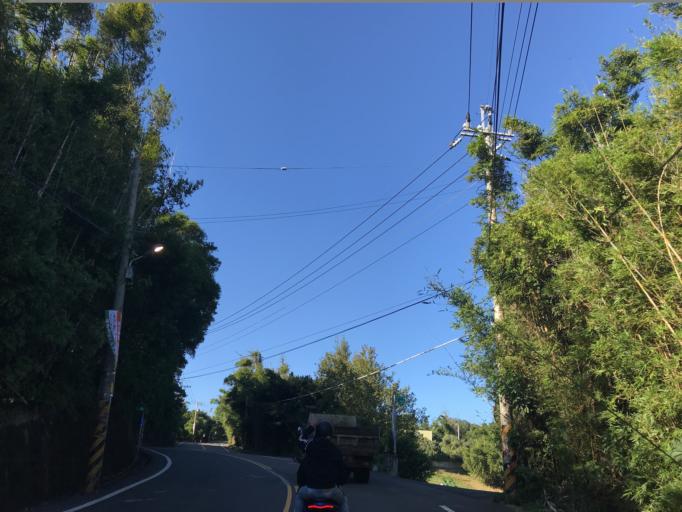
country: TW
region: Taiwan
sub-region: Hsinchu
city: Zhubei
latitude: 24.8621
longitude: 121.0953
